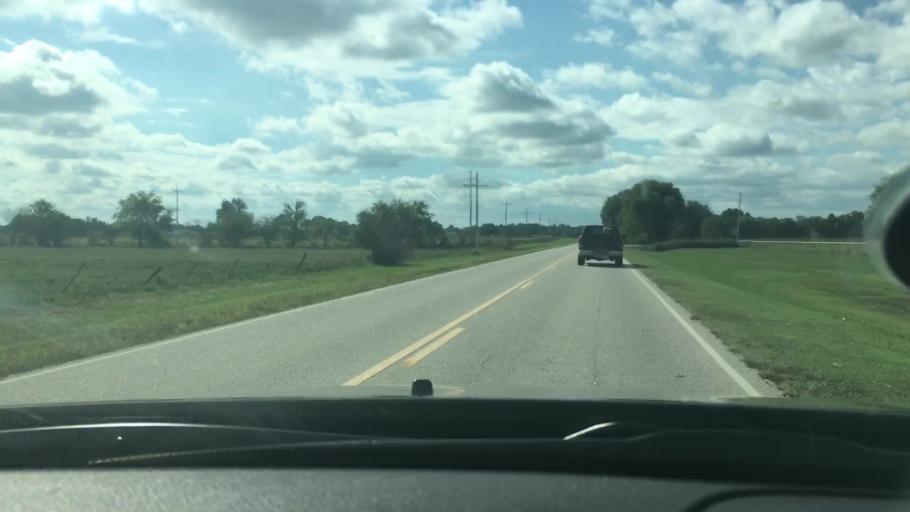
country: US
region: Oklahoma
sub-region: Pontotoc County
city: Ada
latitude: 34.6962
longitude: -96.6349
